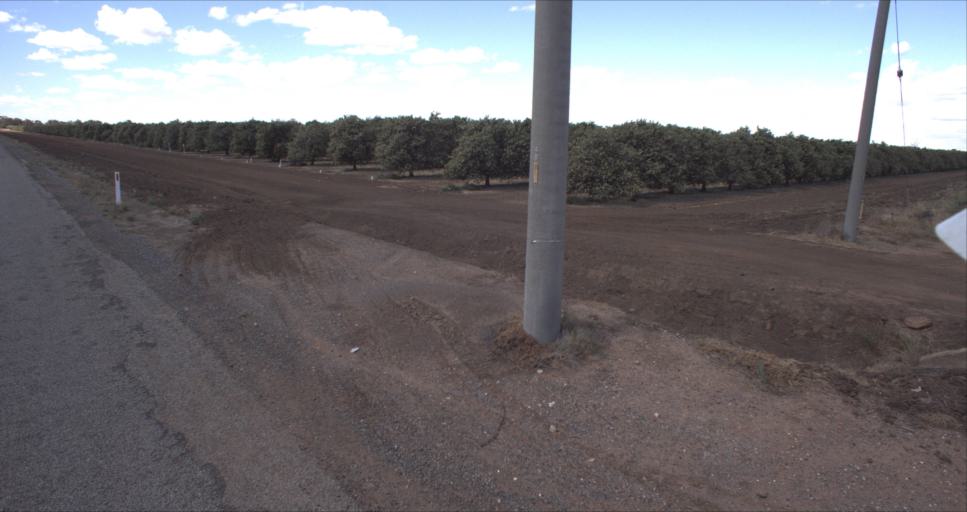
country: AU
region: New South Wales
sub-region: Leeton
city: Leeton
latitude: -34.5245
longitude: 146.2219
